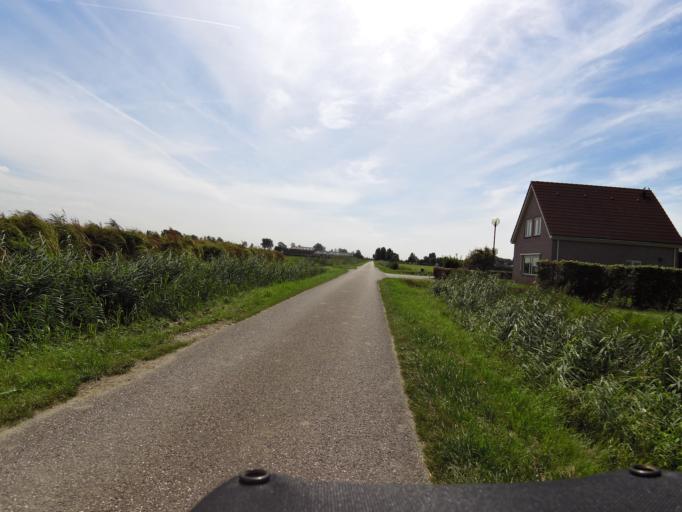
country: NL
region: South Holland
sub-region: Gemeente Goeree-Overflakkee
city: Middelharnis
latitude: 51.7587
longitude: 4.1397
